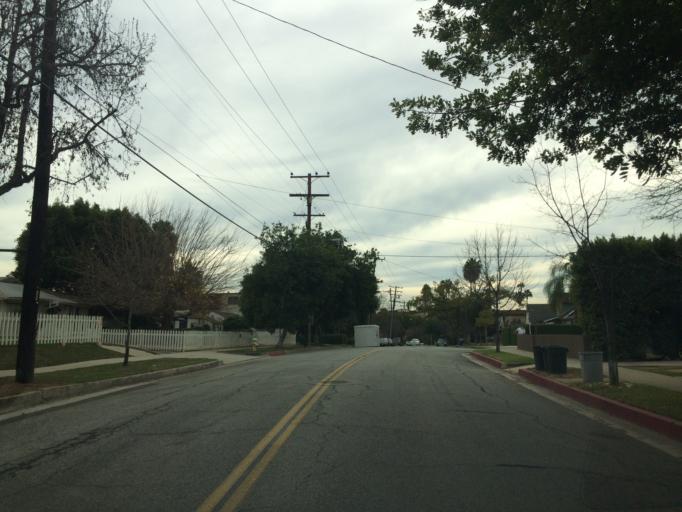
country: US
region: California
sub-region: Los Angeles County
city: South Pasadena
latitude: 34.1006
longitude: -118.1568
